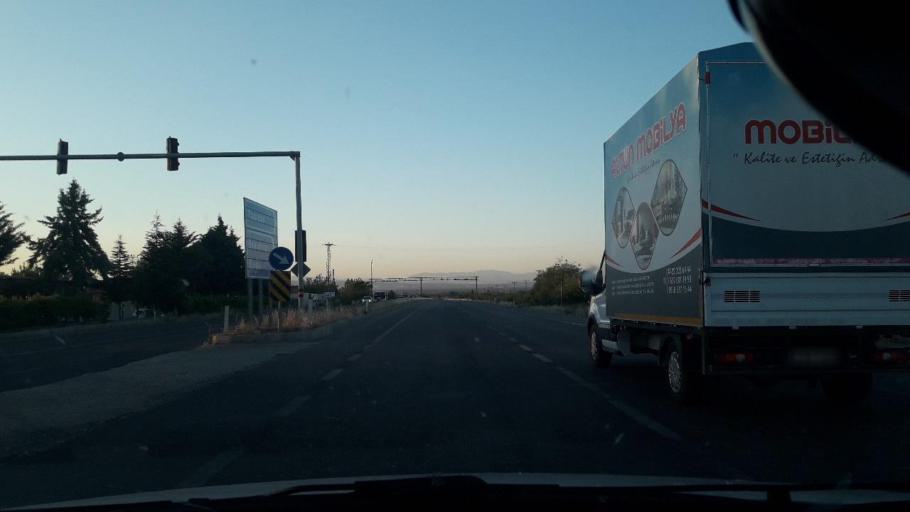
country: TR
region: Malatya
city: Malatya
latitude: 38.4481
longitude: 38.2270
